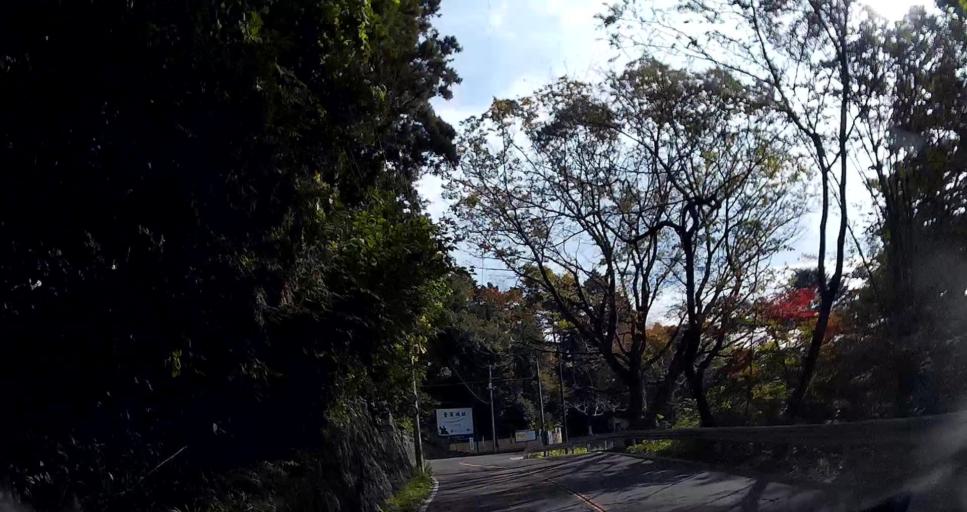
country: JP
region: Miyagi
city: Sendai
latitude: 38.2512
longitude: 140.8546
